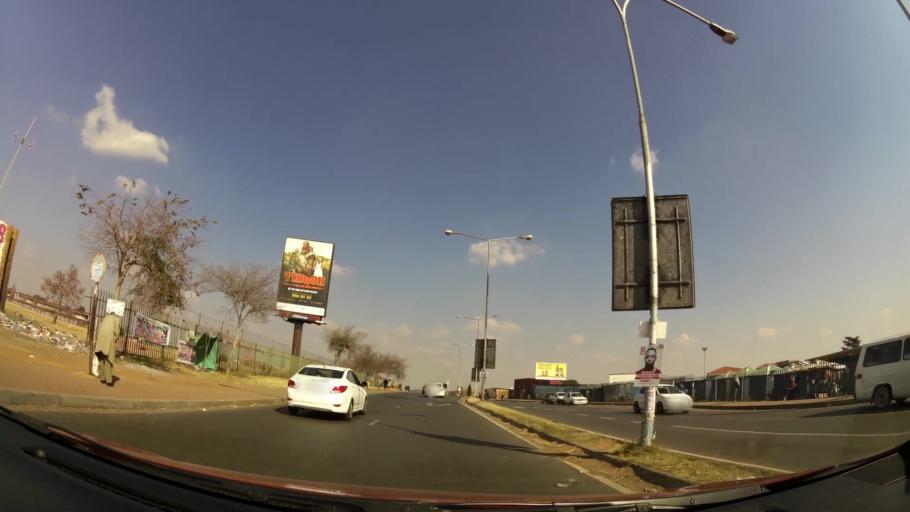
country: ZA
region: Gauteng
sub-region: City of Johannesburg Metropolitan Municipality
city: Soweto
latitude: -26.2431
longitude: 27.9497
